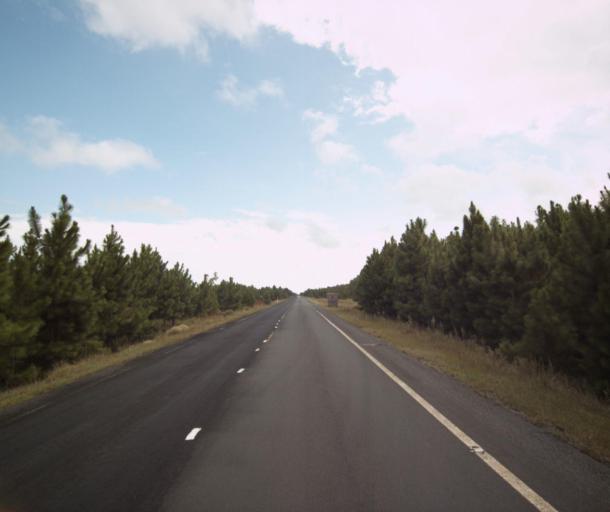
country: BR
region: Rio Grande do Sul
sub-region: Tapes
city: Tapes
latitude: -31.4181
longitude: -51.1763
